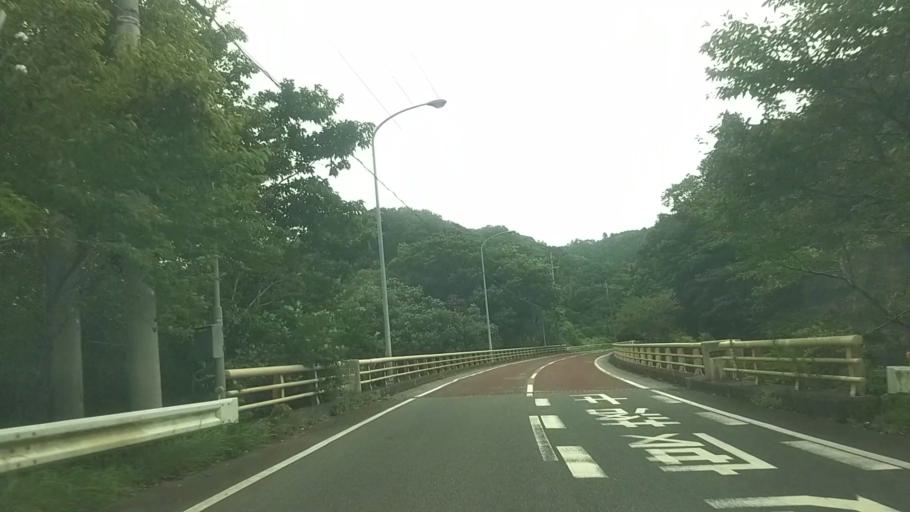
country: JP
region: Chiba
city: Kimitsu
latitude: 35.2359
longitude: 139.9705
